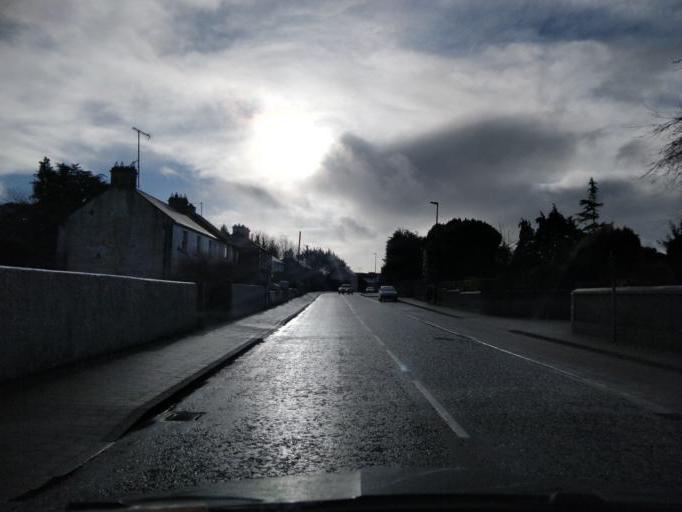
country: IE
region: Connaught
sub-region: Roscommon
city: Roscommon
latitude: 53.6358
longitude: -8.1903
